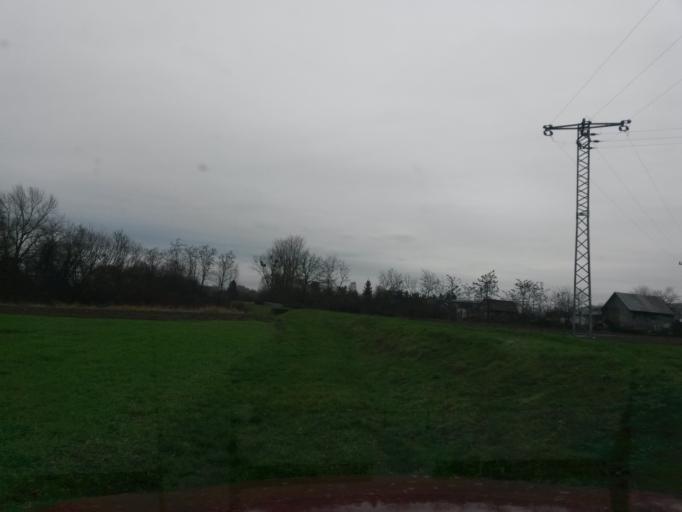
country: UA
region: Zakarpattia
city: Storozhnytsya
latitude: 48.6301
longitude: 22.0994
